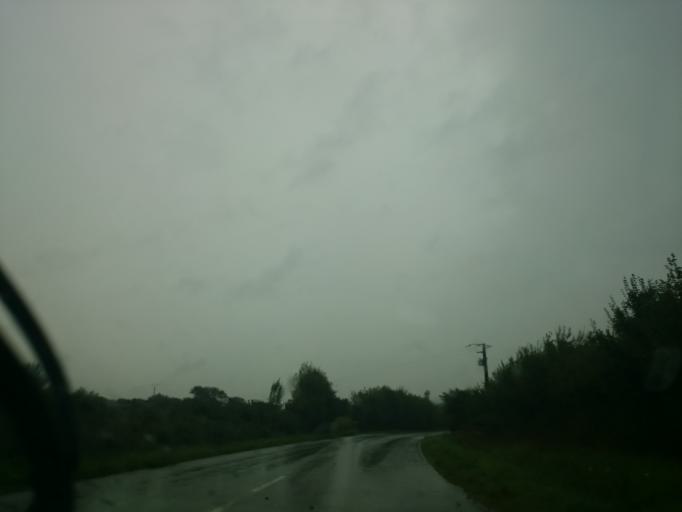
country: FR
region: Brittany
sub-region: Departement du Finistere
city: Plouvien
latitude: 48.5297
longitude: -4.4646
